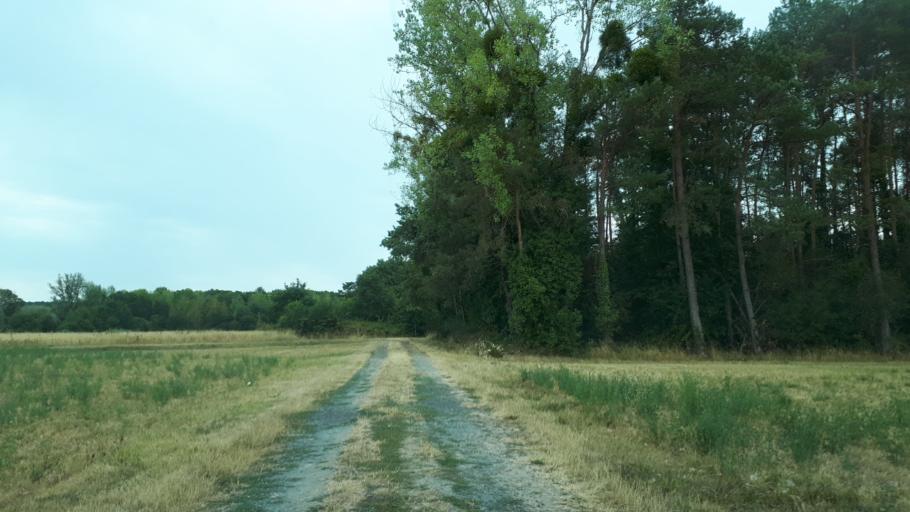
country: FR
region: Centre
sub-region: Departement du Loir-et-Cher
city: Saint-Romain-sur-Cher
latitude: 47.3515
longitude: 1.3963
